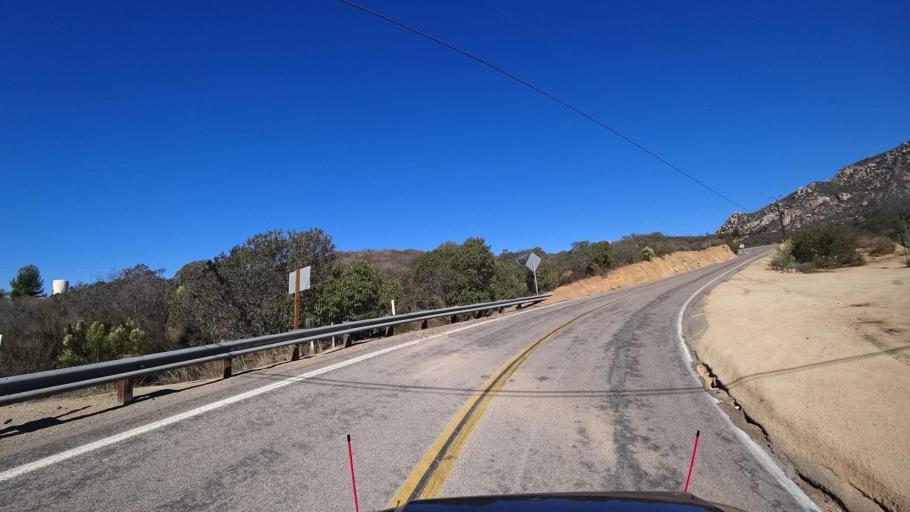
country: US
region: California
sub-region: San Diego County
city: Jamul
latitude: 32.7082
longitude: -116.7984
